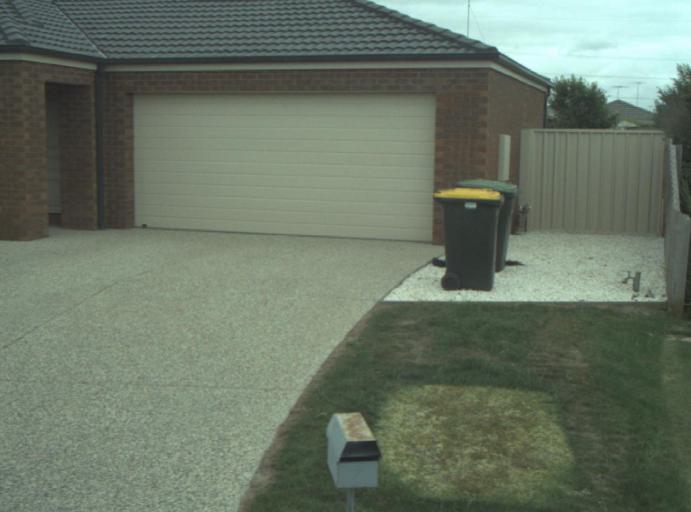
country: AU
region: Victoria
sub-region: Greater Geelong
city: Breakwater
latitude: -38.2014
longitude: 144.3496
